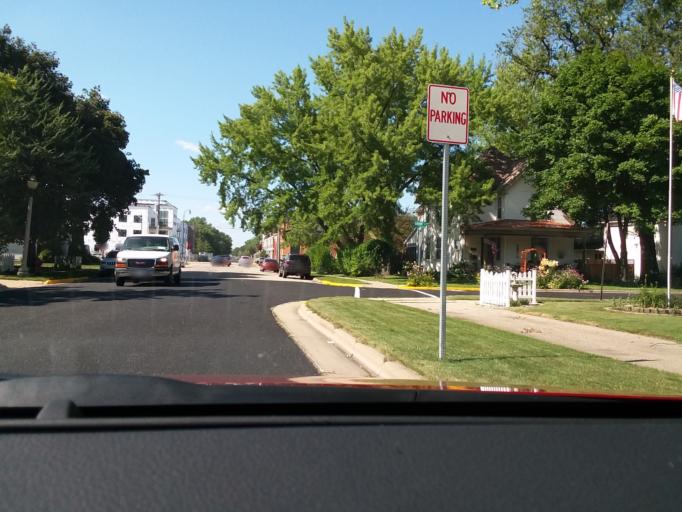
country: US
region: Wisconsin
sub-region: Dane County
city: Waunakee
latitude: 43.1907
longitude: -89.4519
